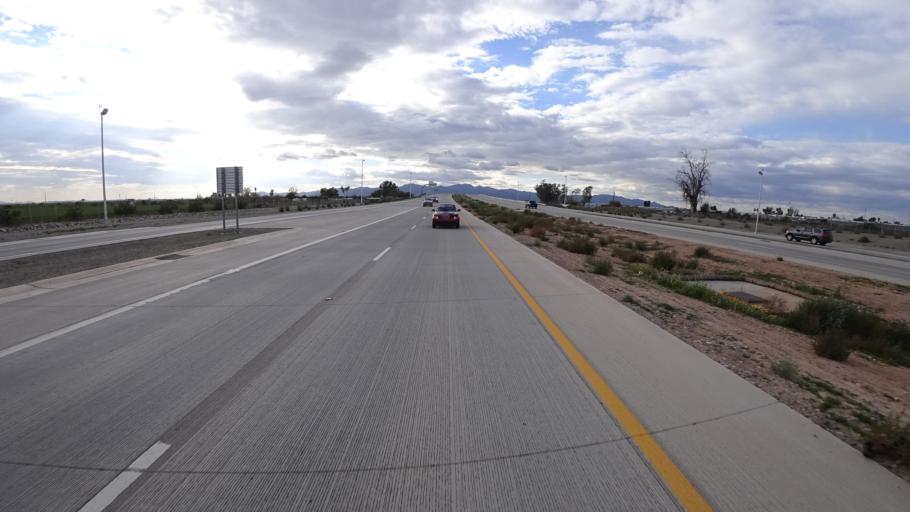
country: US
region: Arizona
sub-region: Maricopa County
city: Litchfield Park
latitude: 33.5577
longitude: -112.3620
